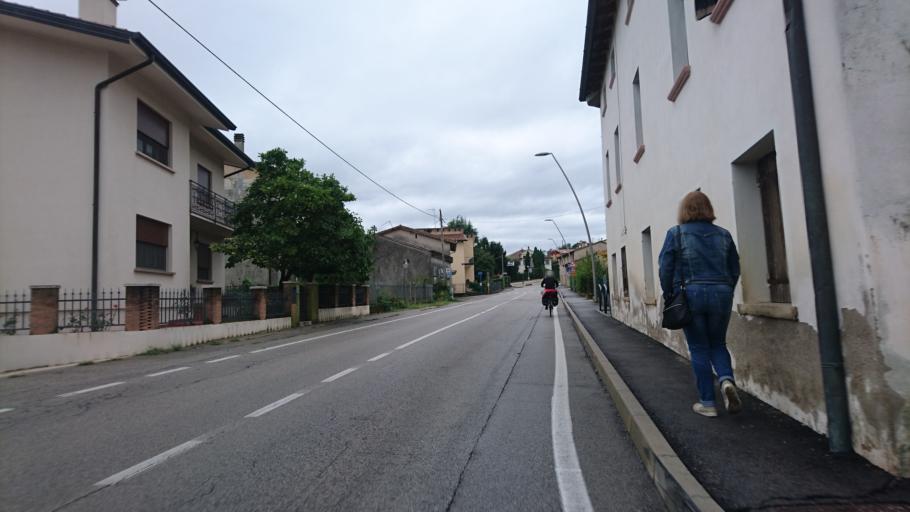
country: IT
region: Veneto
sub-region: Provincia di Treviso
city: Asolo
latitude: 45.7956
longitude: 11.9398
